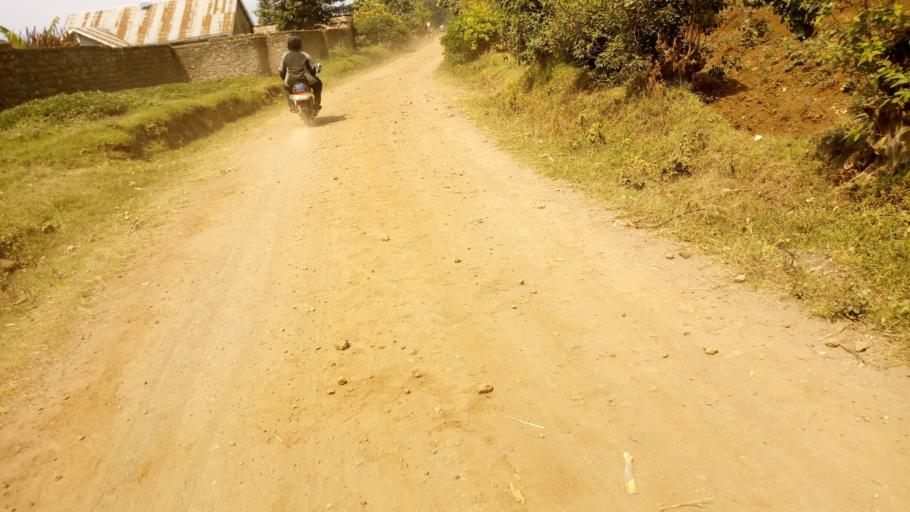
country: UG
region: Western Region
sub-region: Kisoro District
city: Kisoro
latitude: -1.3137
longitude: 29.7124
